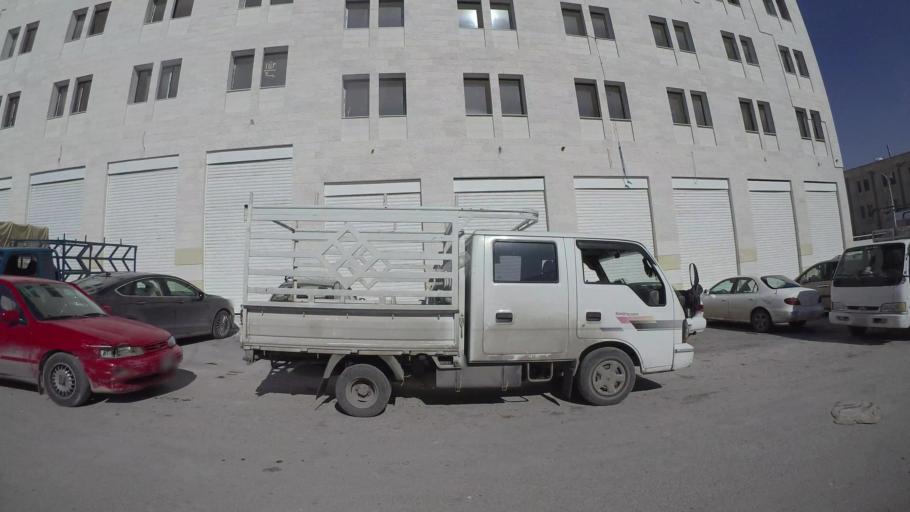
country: JO
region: Zarqa
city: Russeifa
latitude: 32.0296
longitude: 36.0412
